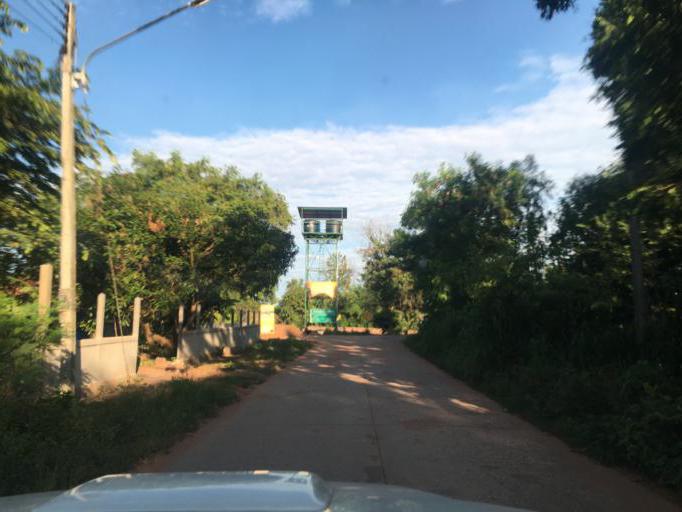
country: TH
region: Changwat Udon Thani
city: Nong Saeng
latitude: 17.2795
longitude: 102.6988
